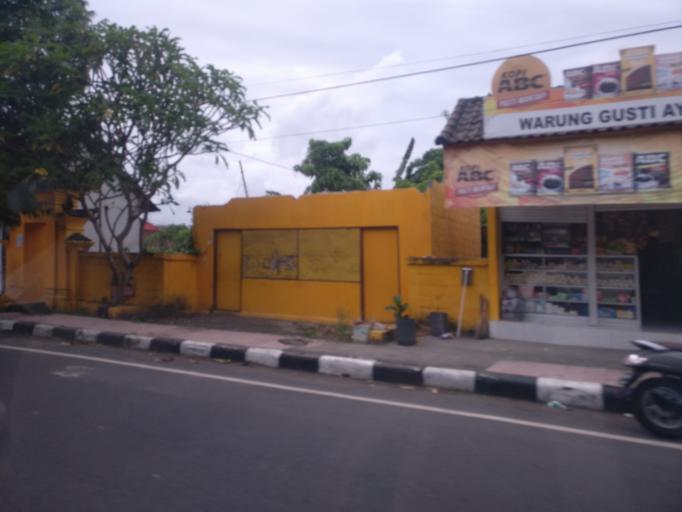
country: ID
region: Bali
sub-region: Kabupaten Gianyar
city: Ubud
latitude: -8.5593
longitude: 115.3016
